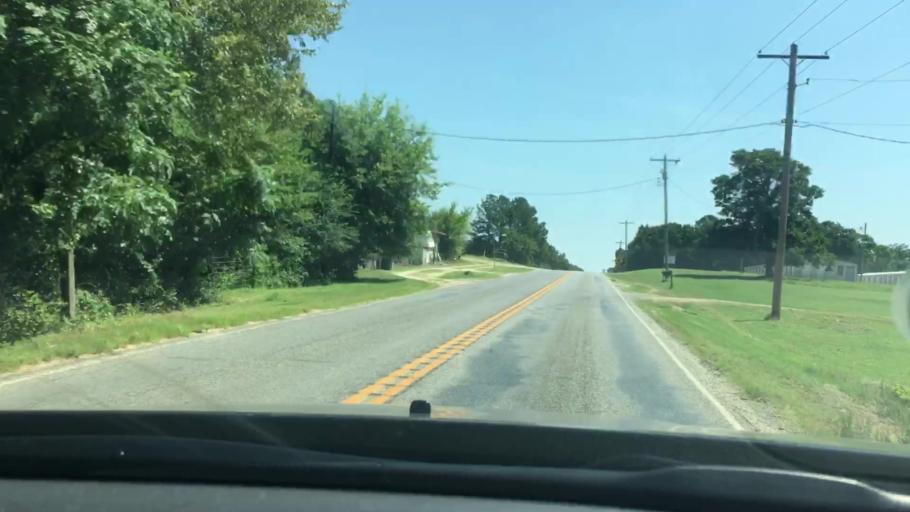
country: US
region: Oklahoma
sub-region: Johnston County
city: Tishomingo
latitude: 34.2377
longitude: -96.6011
